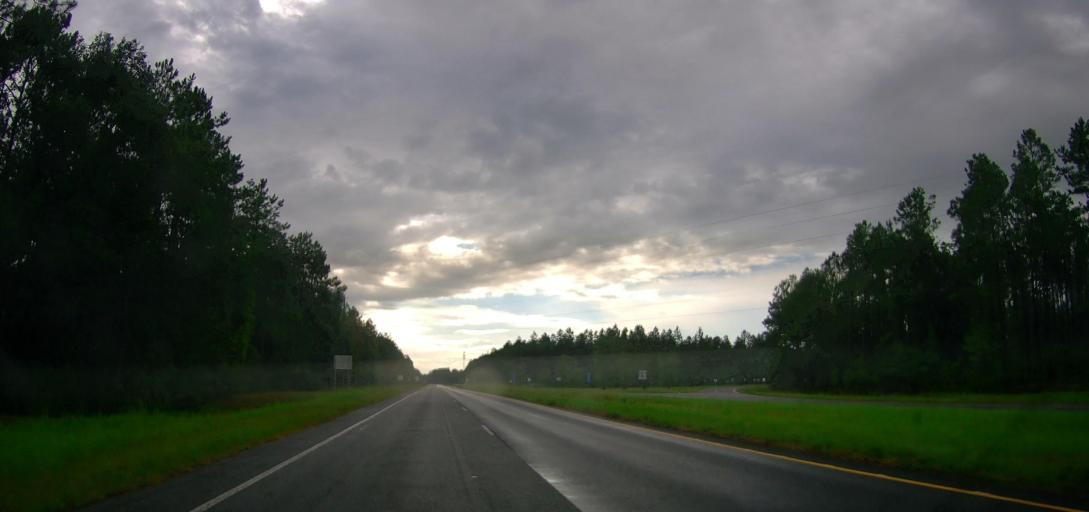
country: US
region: Georgia
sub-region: Ware County
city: Deenwood
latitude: 31.2616
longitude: -82.5159
